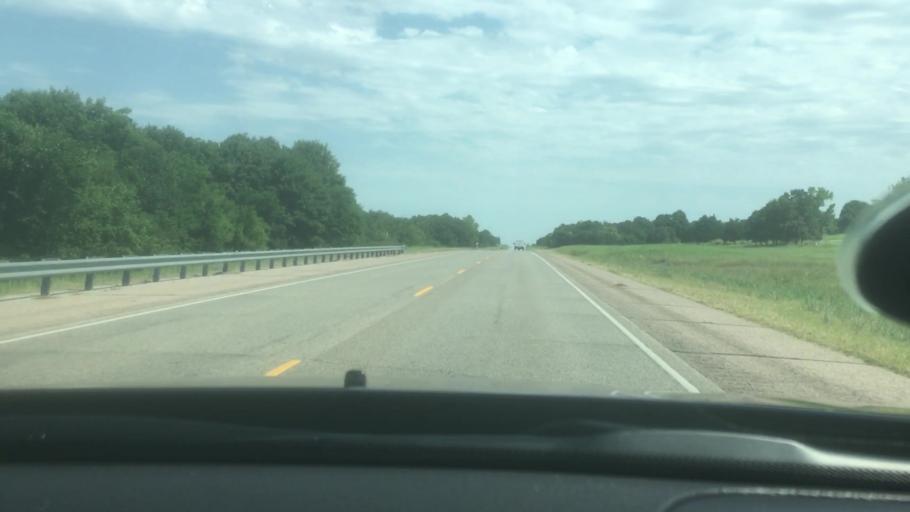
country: US
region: Oklahoma
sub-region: Seminole County
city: Konawa
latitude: 35.0082
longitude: -96.9317
